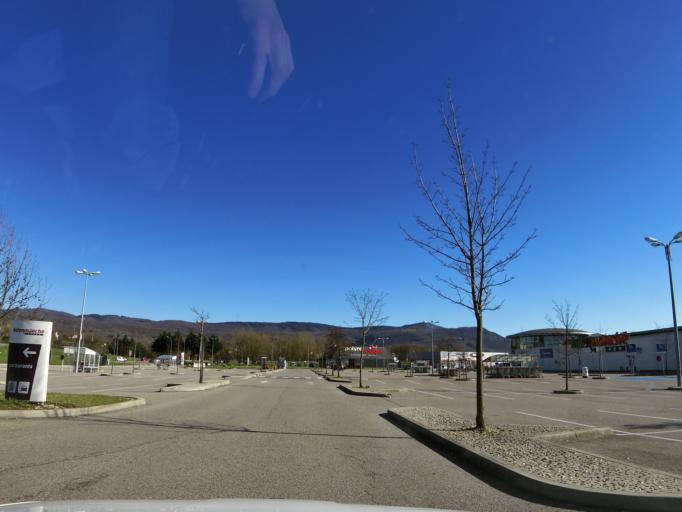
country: FR
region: Rhone-Alpes
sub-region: Departement de l'Ain
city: Amberieu-en-Bugey
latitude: 45.9726
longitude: 5.3376
